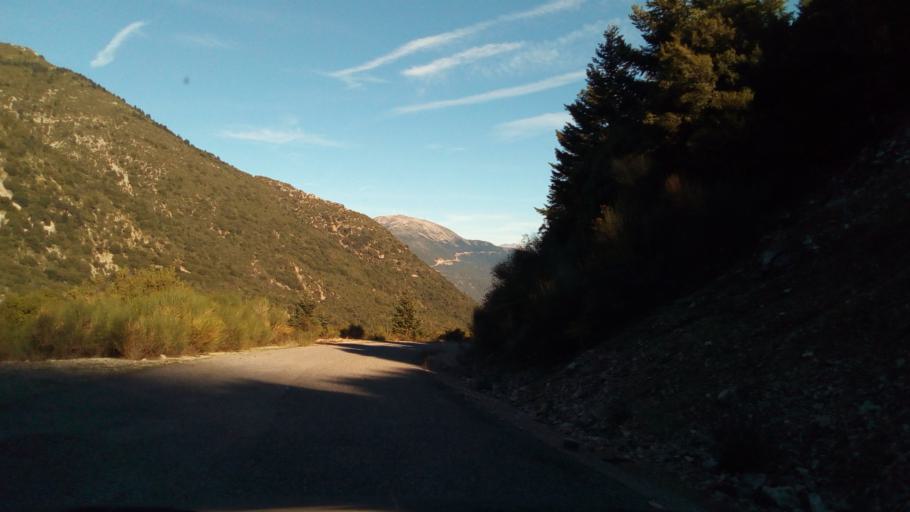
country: GR
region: West Greece
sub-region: Nomos Aitolias kai Akarnanias
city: Nafpaktos
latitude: 38.5442
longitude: 21.8526
